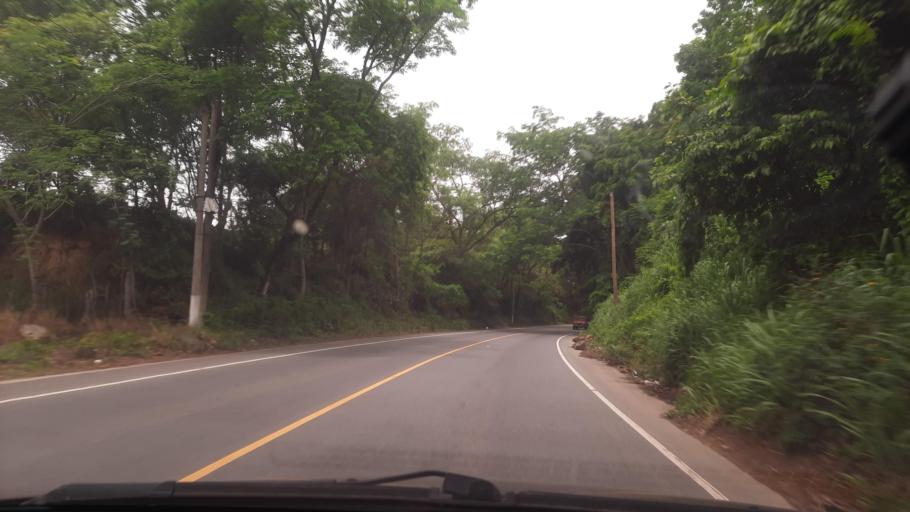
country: GT
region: Zacapa
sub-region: Municipio de Zacapa
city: Gualan
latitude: 15.1862
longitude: -89.2829
